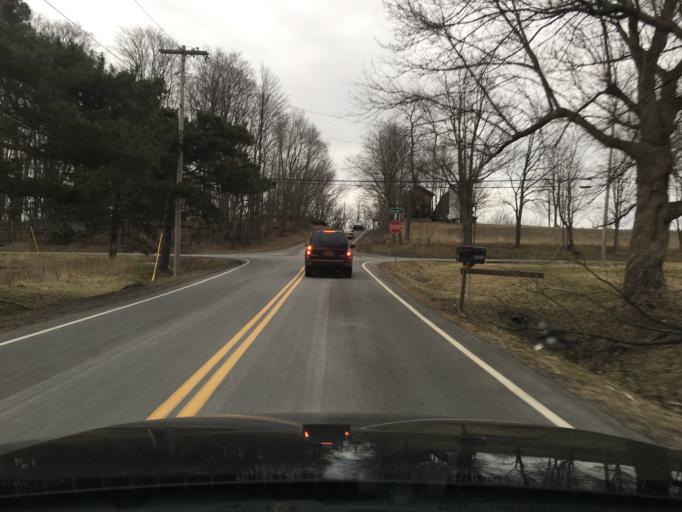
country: US
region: New York
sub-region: Ontario County
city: Victor
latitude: 43.0457
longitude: -77.3821
